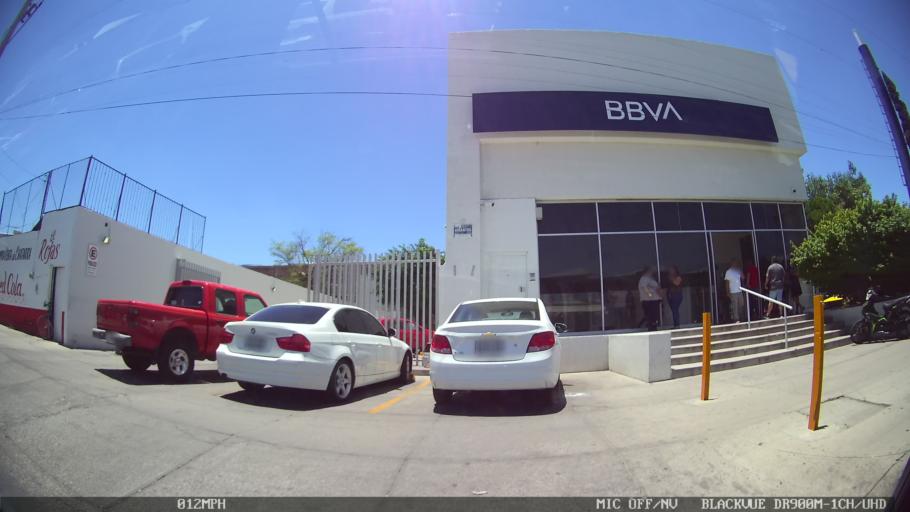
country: MX
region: Jalisco
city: Tlaquepaque
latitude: 20.6614
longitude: -103.2883
